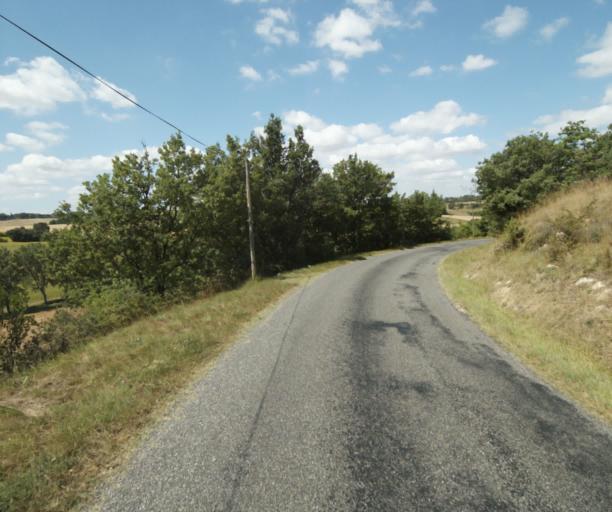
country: FR
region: Midi-Pyrenees
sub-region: Departement de la Haute-Garonne
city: Saint-Felix-Lauragais
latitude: 43.4669
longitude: 1.8539
